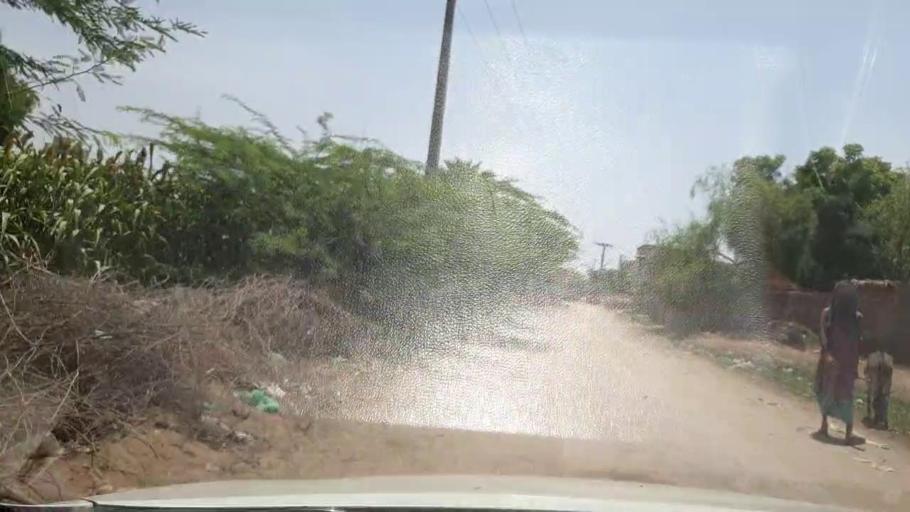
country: PK
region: Sindh
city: Bozdar
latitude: 27.2065
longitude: 68.6661
